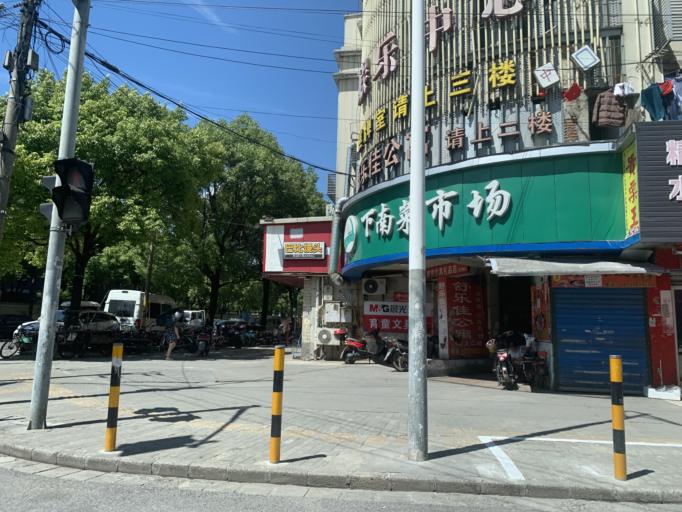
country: CN
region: Shanghai Shi
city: Huamu
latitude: 31.1740
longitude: 121.5359
